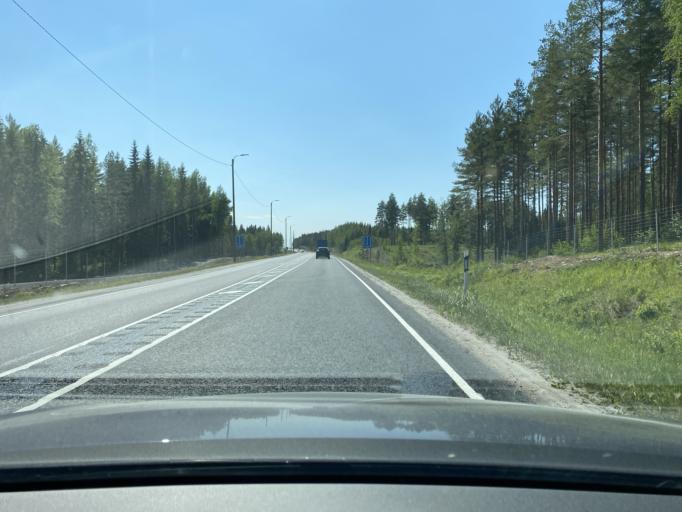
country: FI
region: Pirkanmaa
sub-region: Lounais-Pirkanmaa
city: Mouhijaervi
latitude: 61.3790
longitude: 23.1574
